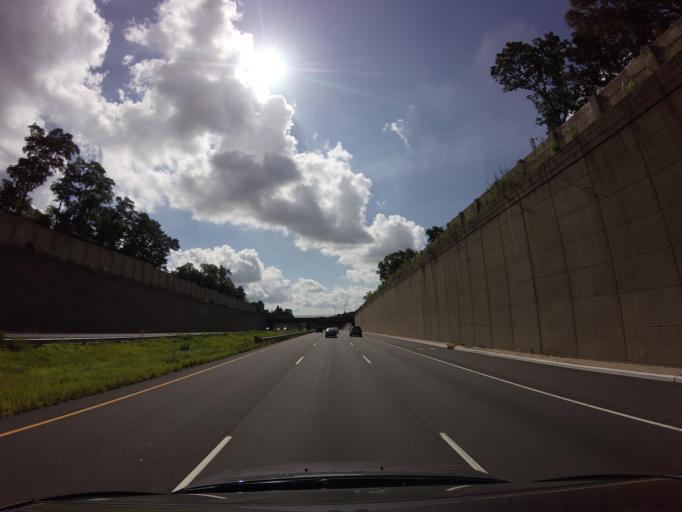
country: US
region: New Jersey
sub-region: Union County
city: Summit
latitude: 40.7283
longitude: -74.3468
